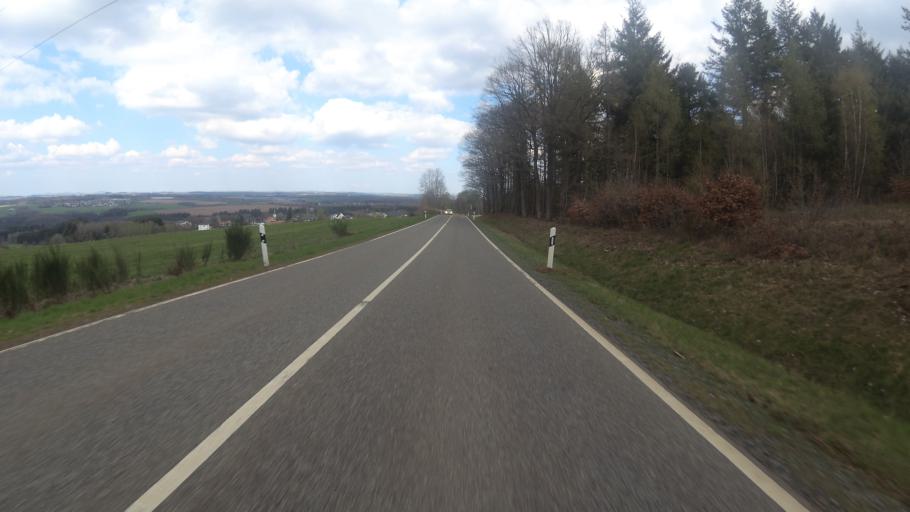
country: DE
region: Rheinland-Pfalz
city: Greimerath
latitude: 50.0340
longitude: 6.9062
